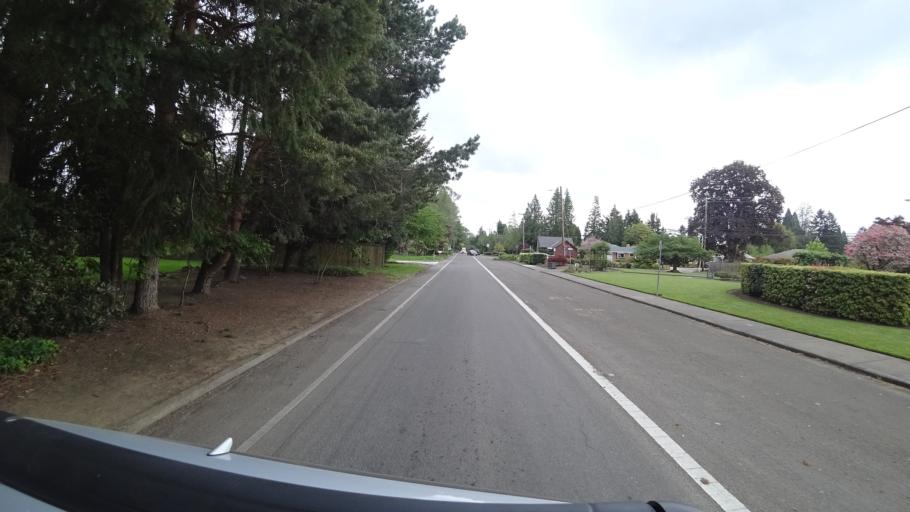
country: US
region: Oregon
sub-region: Washington County
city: Hillsboro
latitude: 45.5285
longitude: -122.9833
